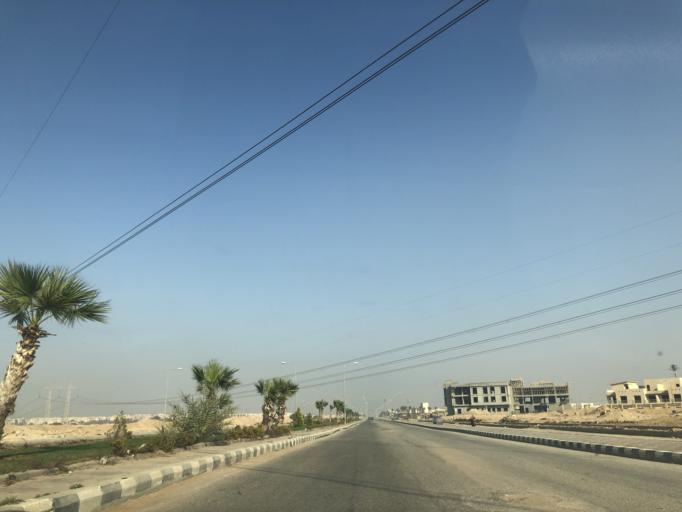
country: EG
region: Al Jizah
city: Madinat Sittah Uktubar
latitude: 29.9419
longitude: 31.0576
